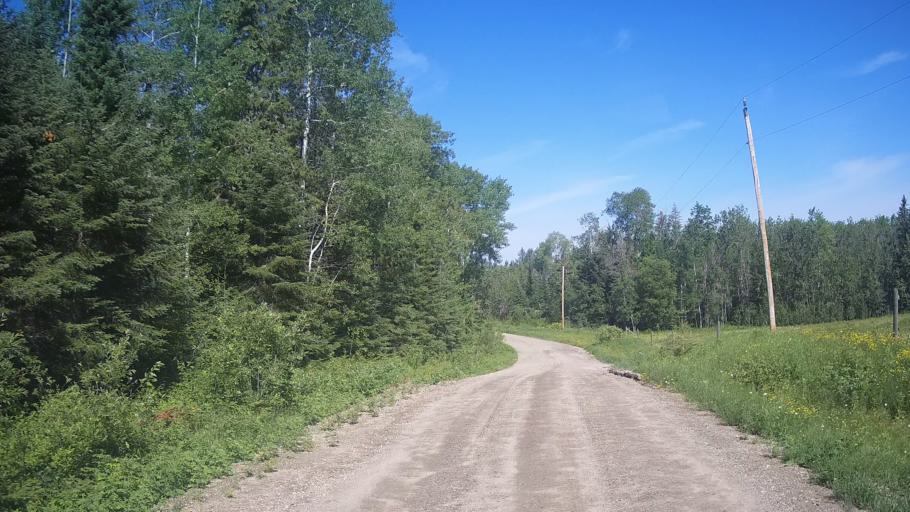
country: CA
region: Ontario
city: Dryden
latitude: 49.8168
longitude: -93.3302
